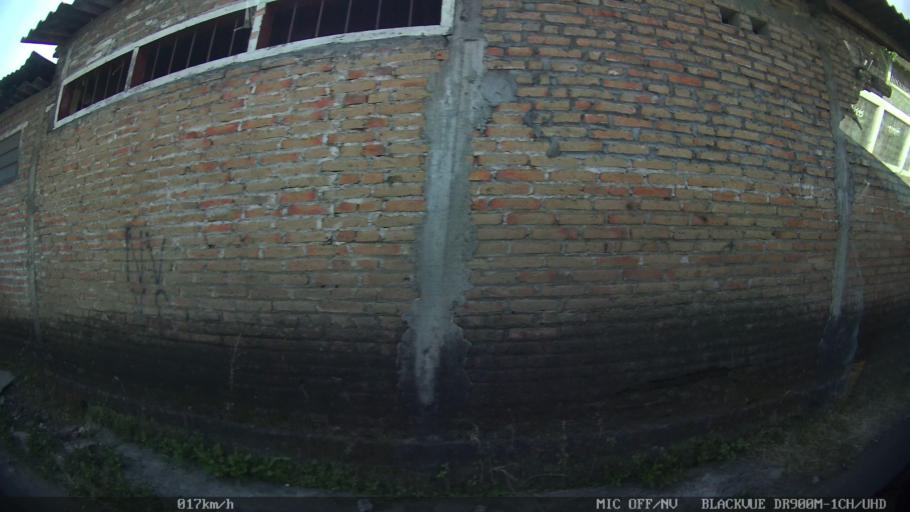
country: ID
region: Daerah Istimewa Yogyakarta
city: Sewon
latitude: -7.8315
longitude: 110.4021
